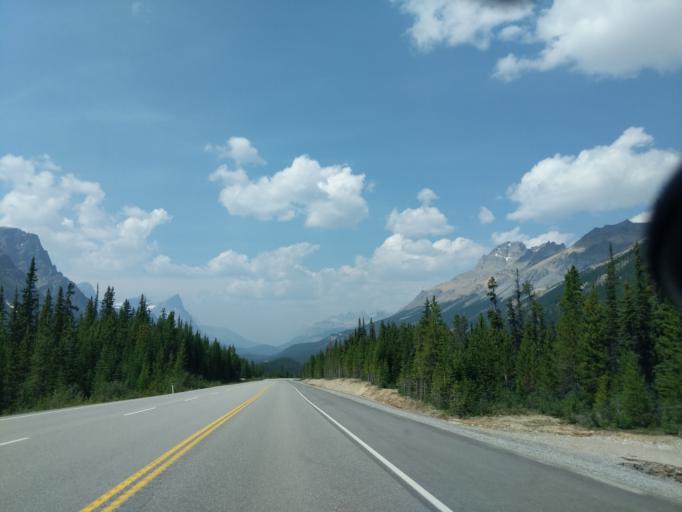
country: CA
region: Alberta
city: Lake Louise
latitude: 51.7370
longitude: -116.5086
